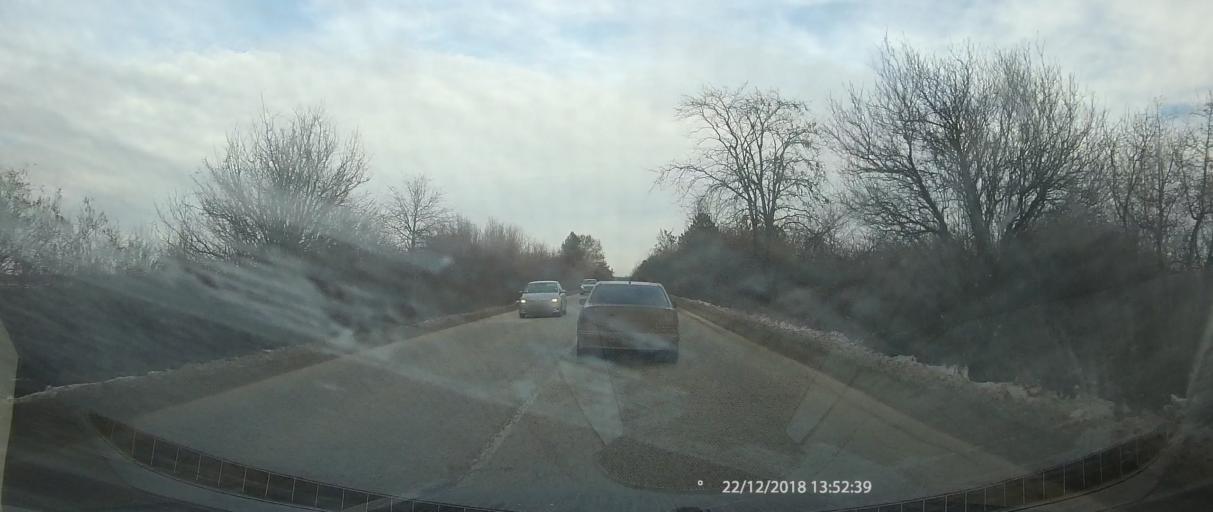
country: BG
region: Pleven
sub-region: Obshtina Cherven Bryag
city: Koynare
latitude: 43.2988
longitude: 24.2381
